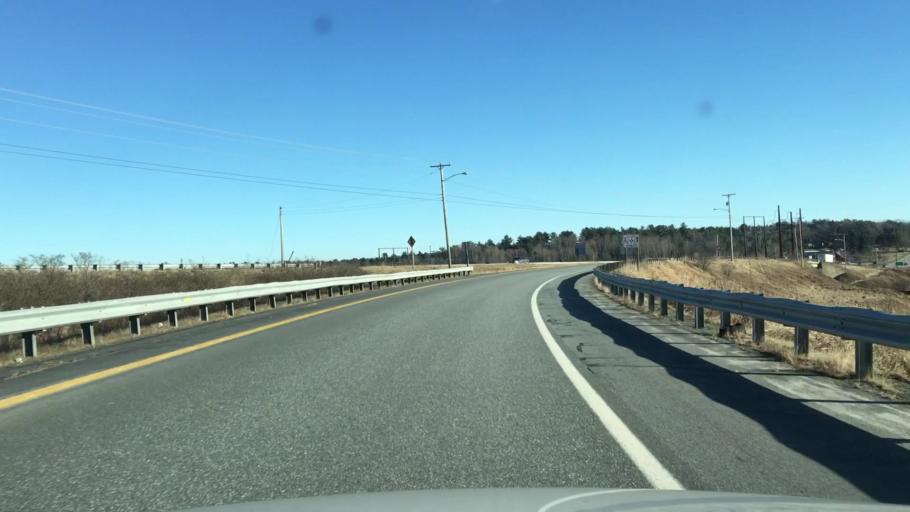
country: US
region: Maine
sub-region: Penobscot County
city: Holden
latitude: 44.7704
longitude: -68.7209
